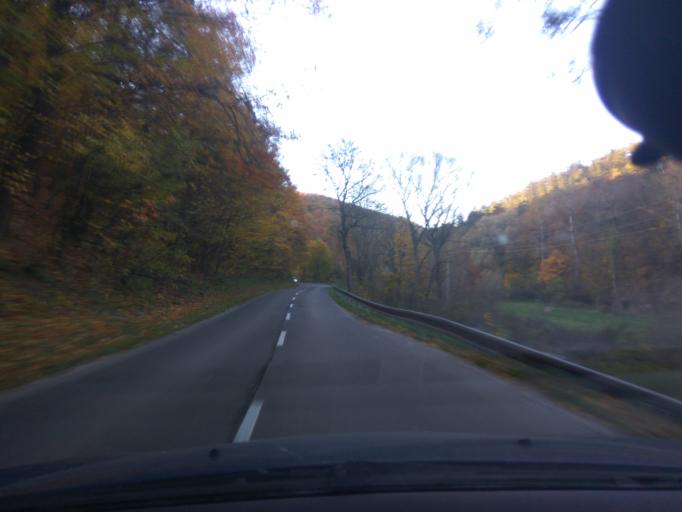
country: SK
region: Nitriansky
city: Brezova pod Bradlom
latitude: 48.6545
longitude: 17.6190
